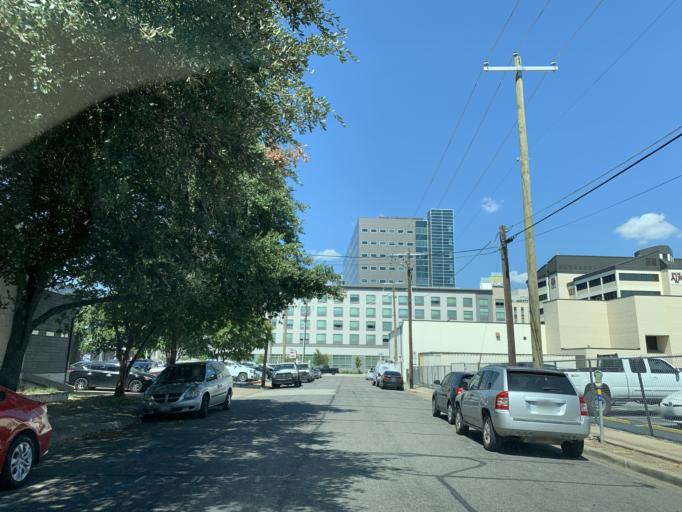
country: US
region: Texas
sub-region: Dallas County
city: Dallas
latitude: 32.7892
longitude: -96.7833
